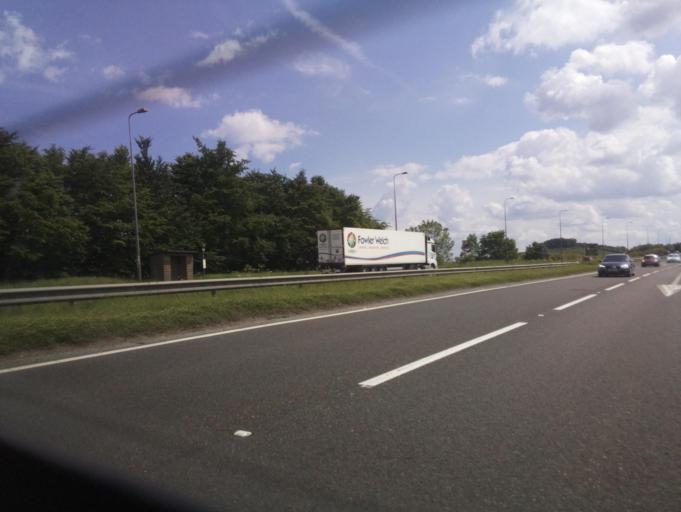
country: GB
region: England
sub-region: County Durham
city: Peterlee
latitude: 54.7199
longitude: -1.3291
